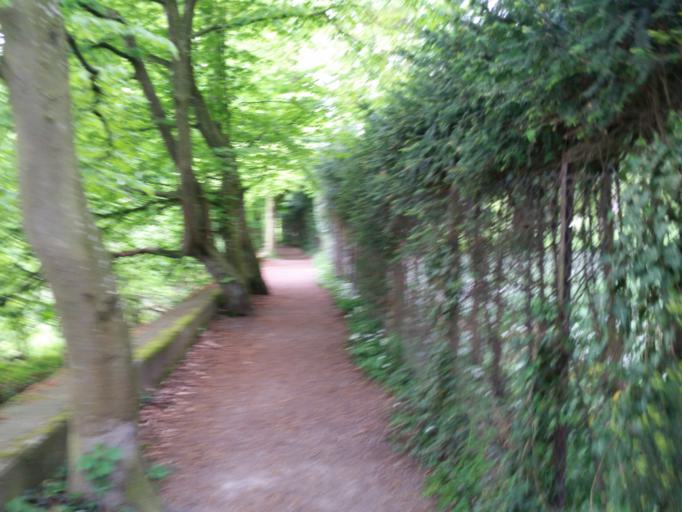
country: CH
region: Thurgau
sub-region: Kreuzlingen District
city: Guttingen
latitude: 47.6039
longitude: 9.3085
